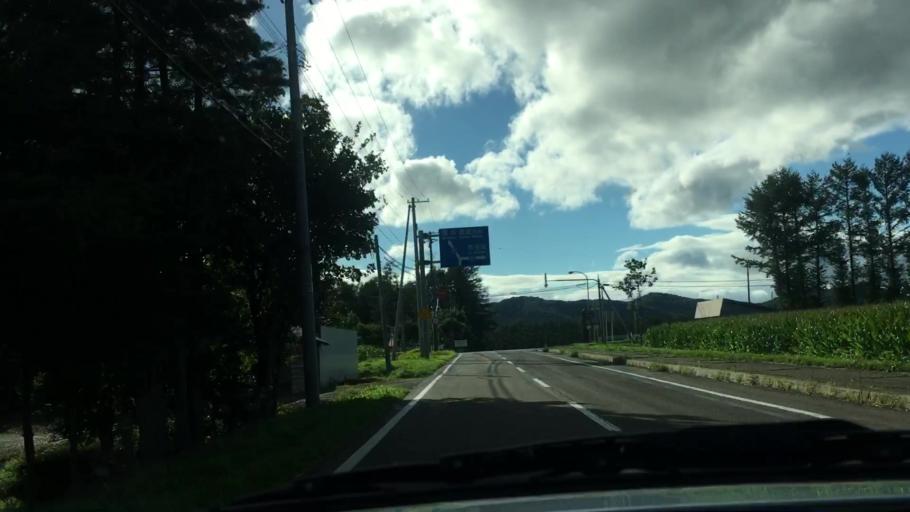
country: JP
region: Hokkaido
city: Otofuke
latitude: 43.1861
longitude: 143.0259
